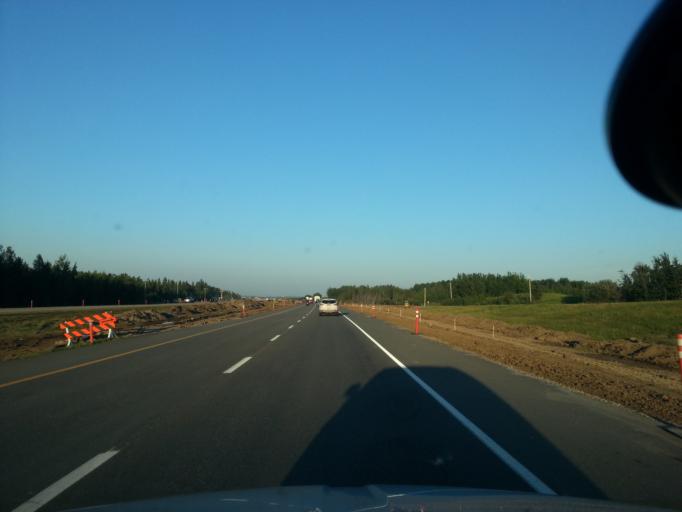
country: CA
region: Alberta
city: Stony Plain
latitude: 53.5699
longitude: -114.0550
